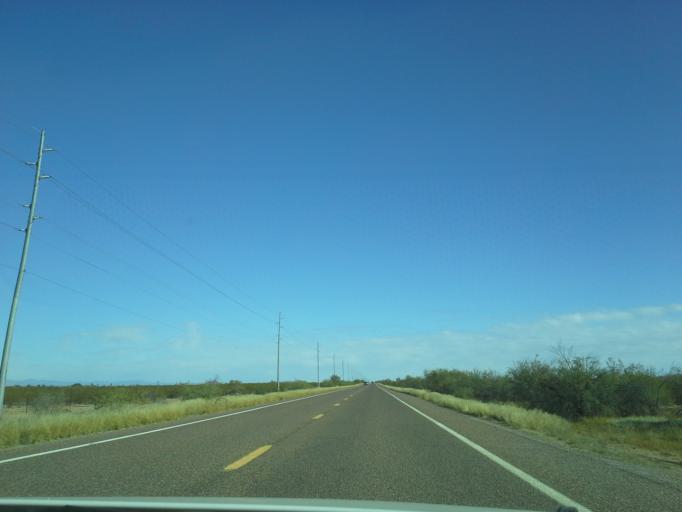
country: US
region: Arizona
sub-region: Yavapai County
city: Congress
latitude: 33.9430
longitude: -113.0639
